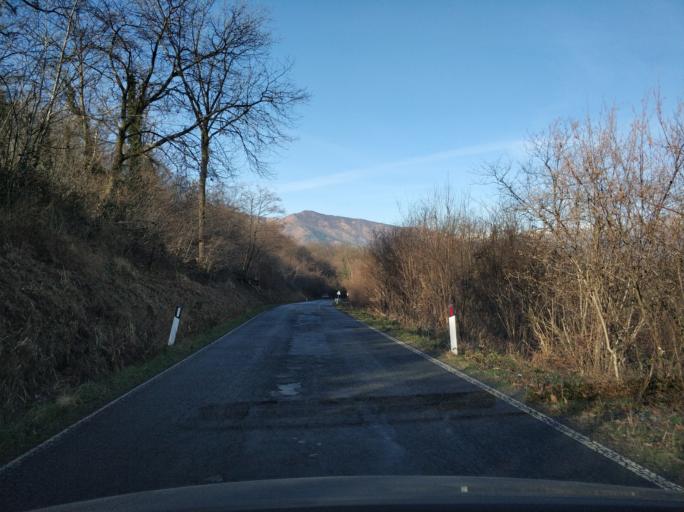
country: IT
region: Piedmont
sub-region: Provincia di Torino
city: Robassomero
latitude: 45.2116
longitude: 7.5505
